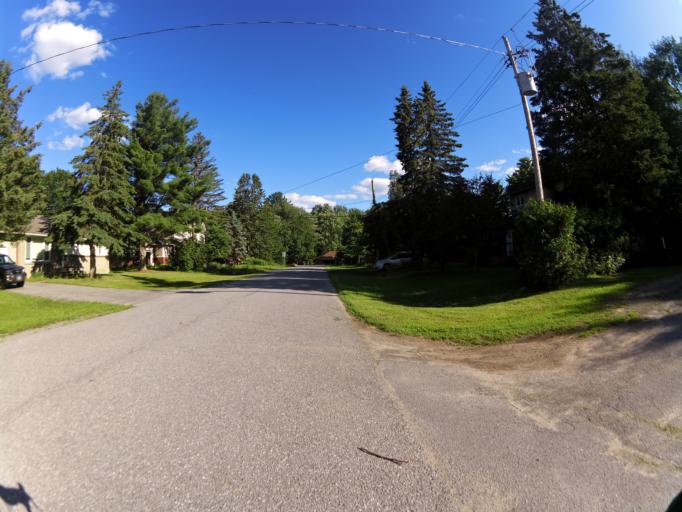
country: CA
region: Ontario
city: Bells Corners
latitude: 45.3237
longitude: -75.7354
